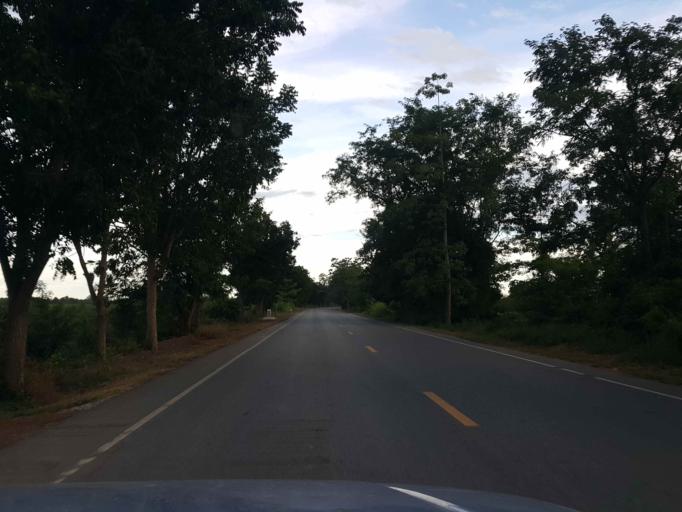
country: TH
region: Sukhothai
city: Sawankhalok
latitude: 17.3738
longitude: 99.7401
